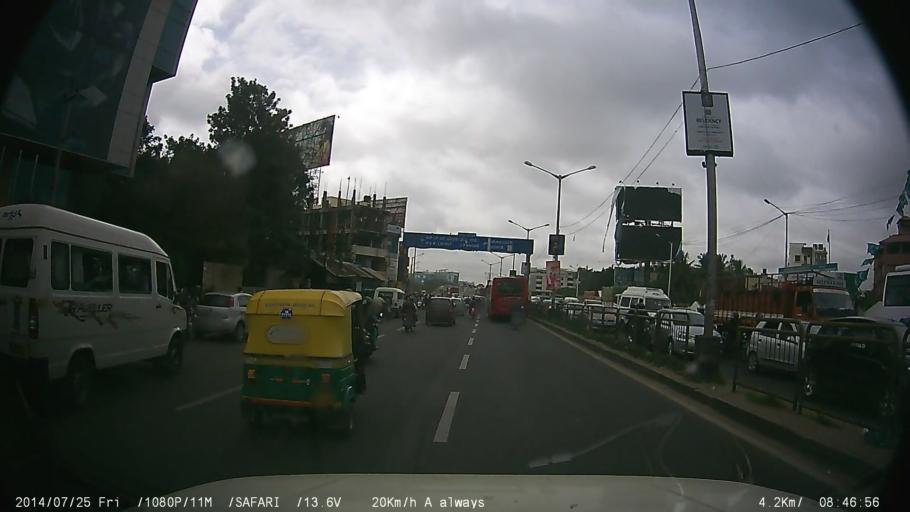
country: IN
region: Karnataka
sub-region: Bangalore Urban
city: Bangalore
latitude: 12.9204
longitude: 77.6207
